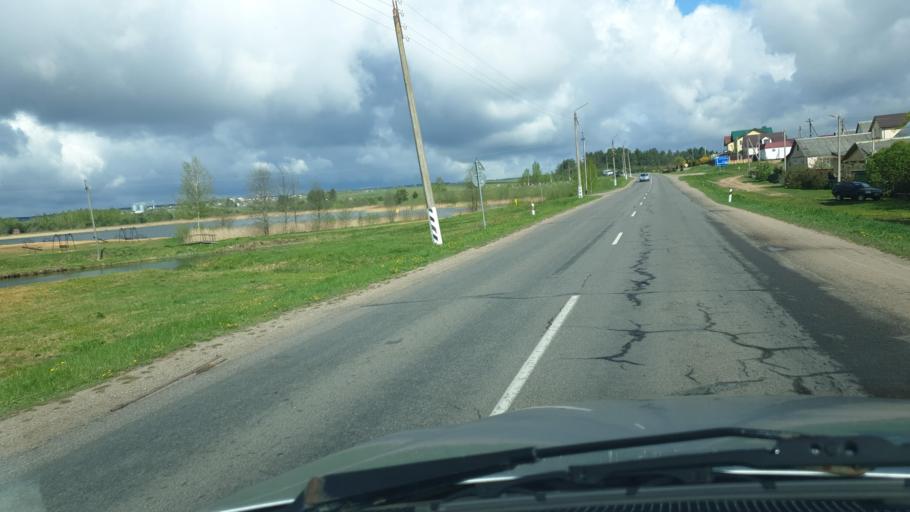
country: BY
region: Vitebsk
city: Lyepyel'
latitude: 54.8805
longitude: 28.6584
